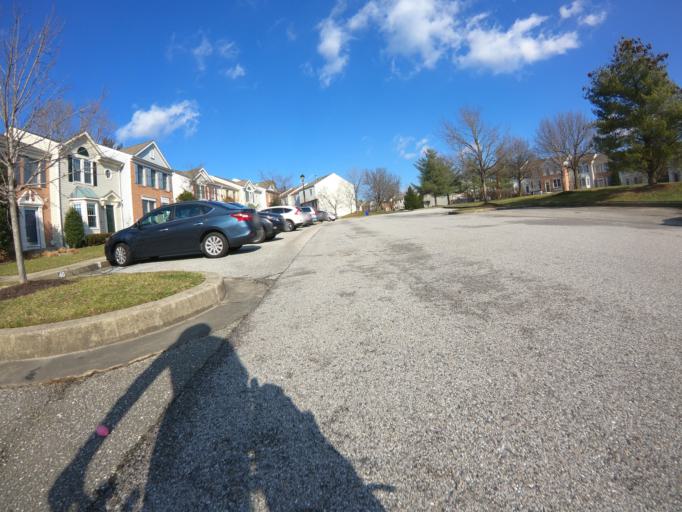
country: US
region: Maryland
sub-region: Howard County
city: Ilchester
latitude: 39.2101
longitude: -76.7880
